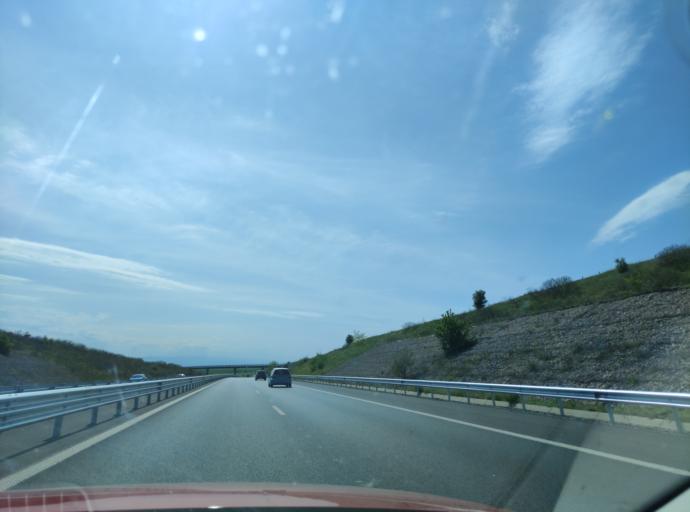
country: BG
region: Stara Zagora
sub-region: Obshtina Chirpan
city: Chirpan
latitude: 42.2022
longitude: 25.2849
